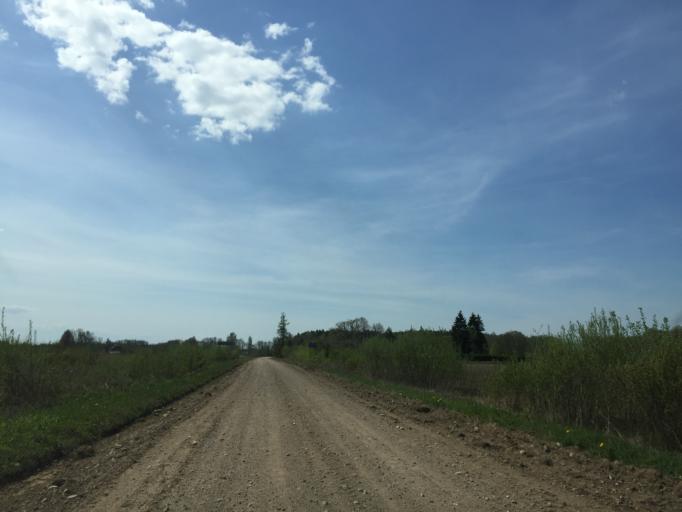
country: LV
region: Limbazu Rajons
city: Limbazi
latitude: 57.3867
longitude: 24.5914
